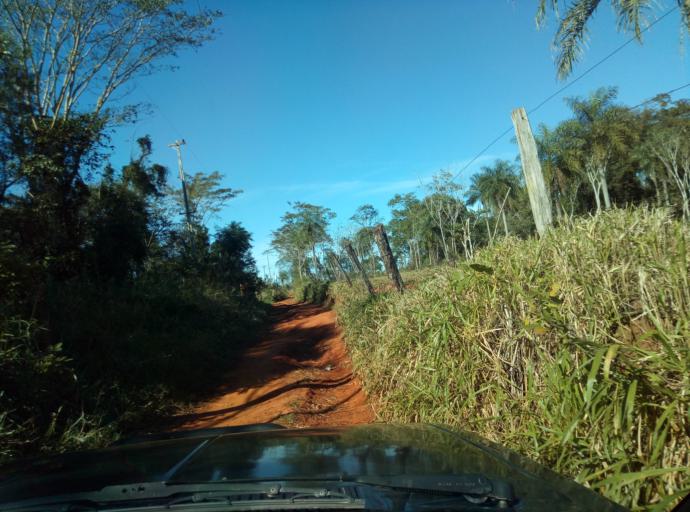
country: PY
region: Caaguazu
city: Doctor Cecilio Baez
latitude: -25.1809
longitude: -56.2423
